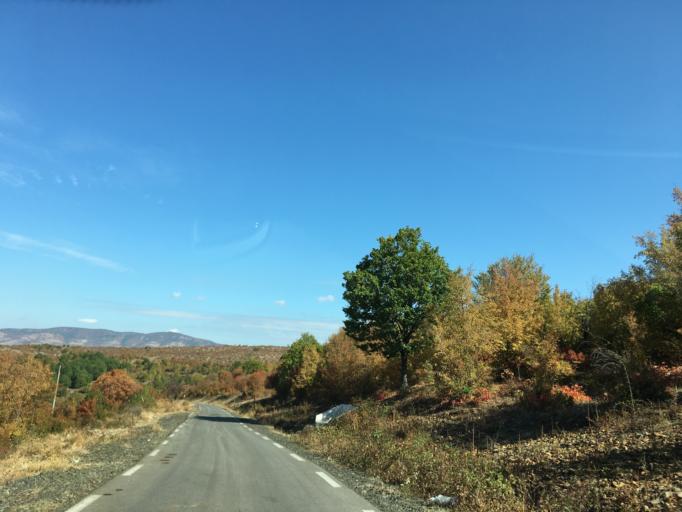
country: BG
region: Kurdzhali
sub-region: Obshtina Krumovgrad
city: Krumovgrad
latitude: 41.5110
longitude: 25.5299
